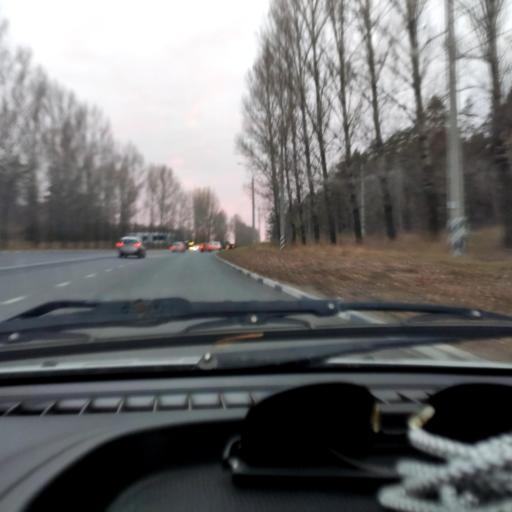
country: RU
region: Samara
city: Zhigulevsk
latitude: 53.5057
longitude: 49.4665
